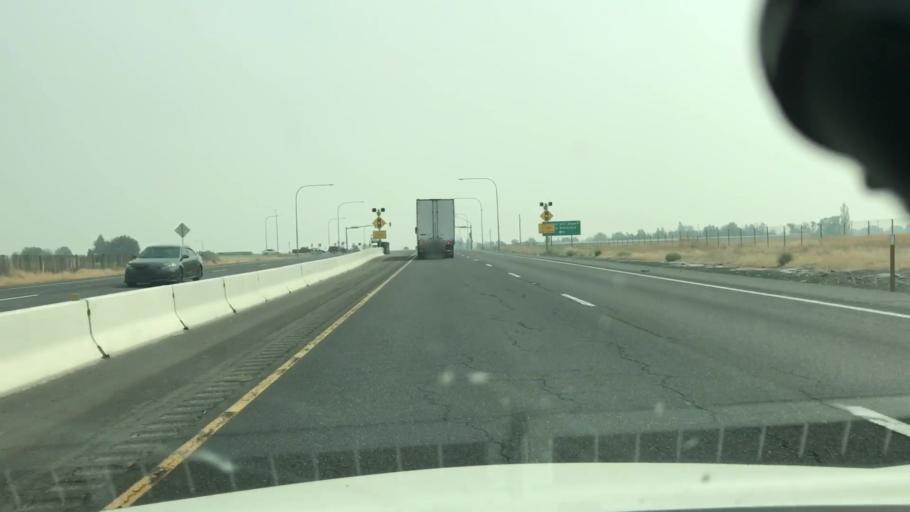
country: US
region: Washington
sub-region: Grant County
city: Cascade Valley
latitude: 47.1576
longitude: -119.3143
